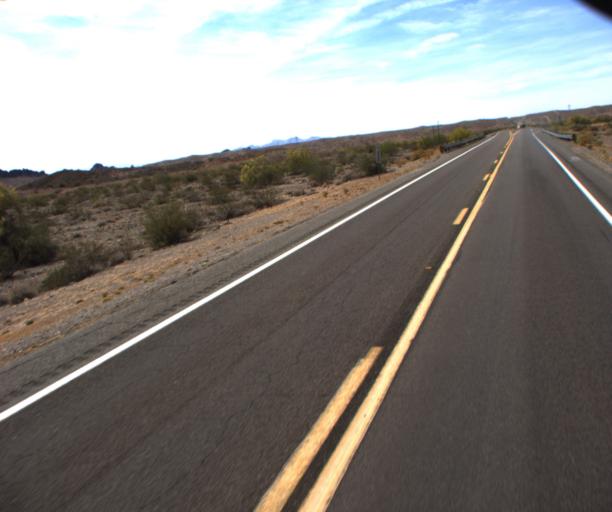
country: US
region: Arizona
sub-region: Mohave County
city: Lake Havasu City
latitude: 34.4144
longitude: -114.1940
